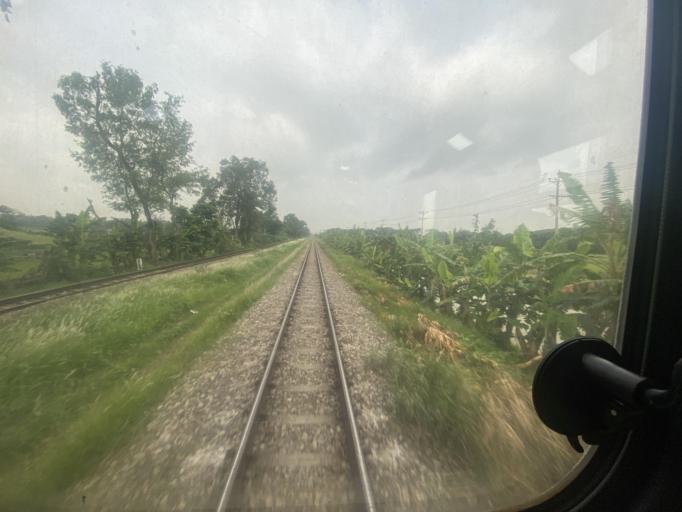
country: BD
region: Dhaka
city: Tungi
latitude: 23.9326
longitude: 90.5159
